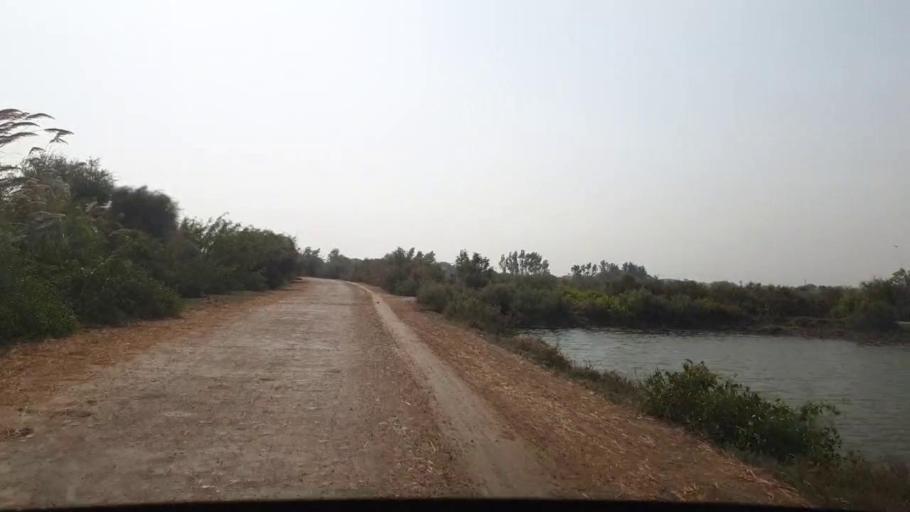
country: PK
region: Sindh
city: Chuhar Jamali
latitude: 24.3754
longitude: 67.9411
